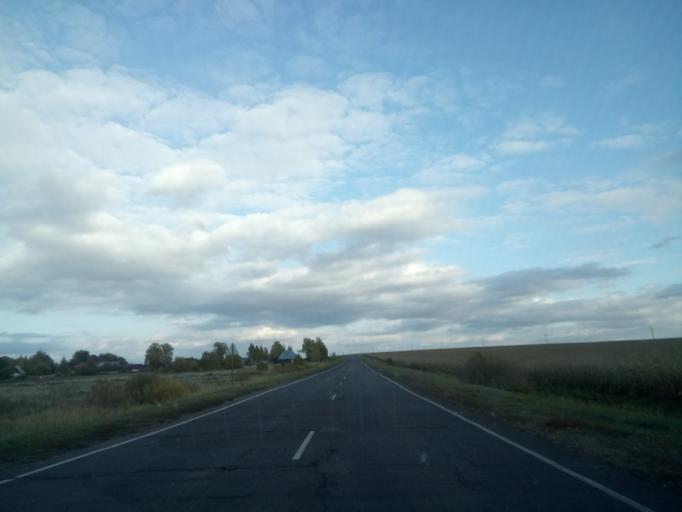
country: RU
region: Nizjnij Novgorod
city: Bol'shoye Boldino
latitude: 54.9907
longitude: 45.3114
